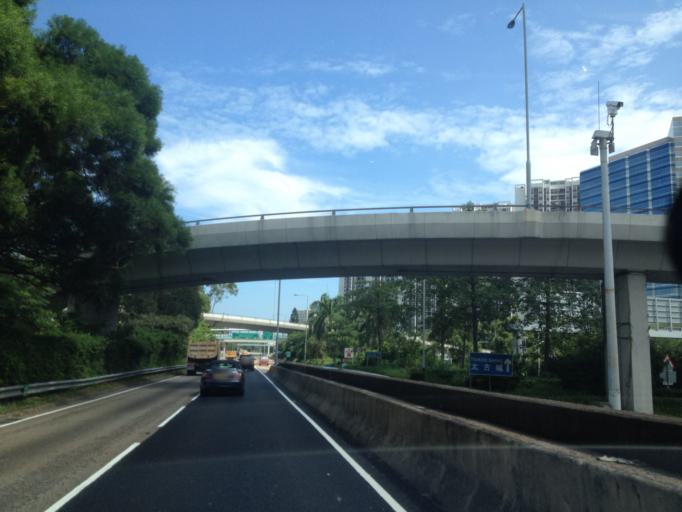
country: HK
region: Kowloon City
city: Kowloon
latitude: 22.2894
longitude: 114.2165
